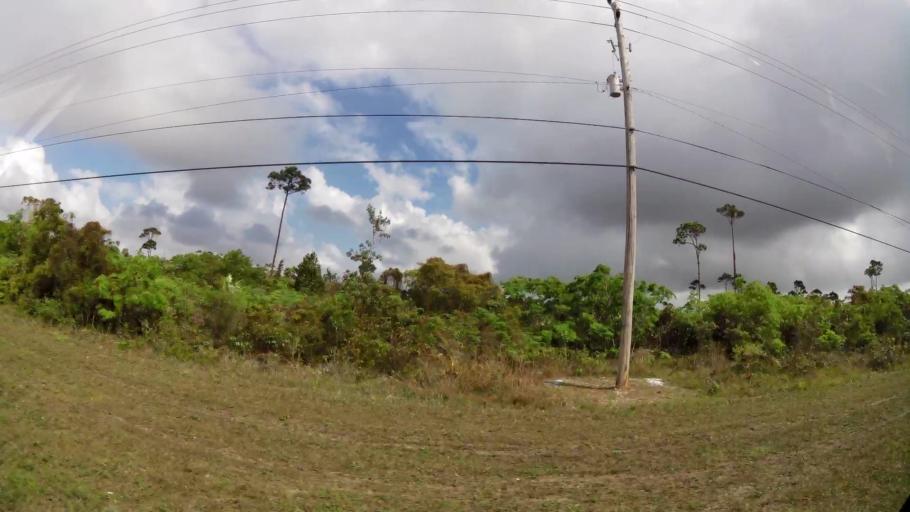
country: BS
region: Freeport
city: Lucaya
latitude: 26.5497
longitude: -78.5761
